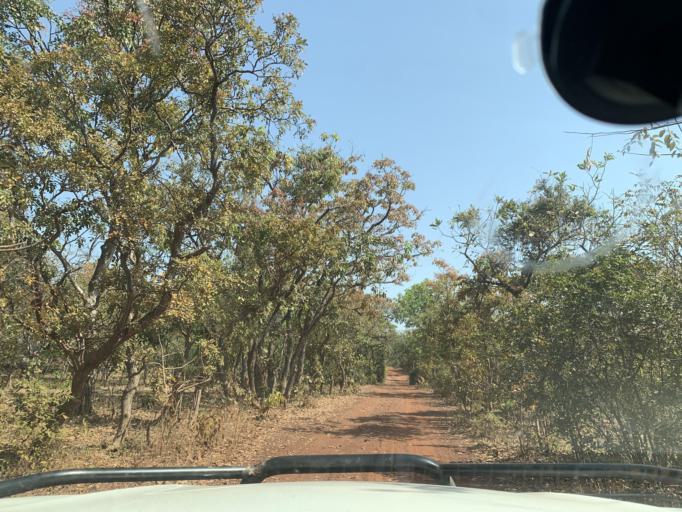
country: ML
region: Sikasso
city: Kolondieba
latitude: 10.8948
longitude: -6.7459
